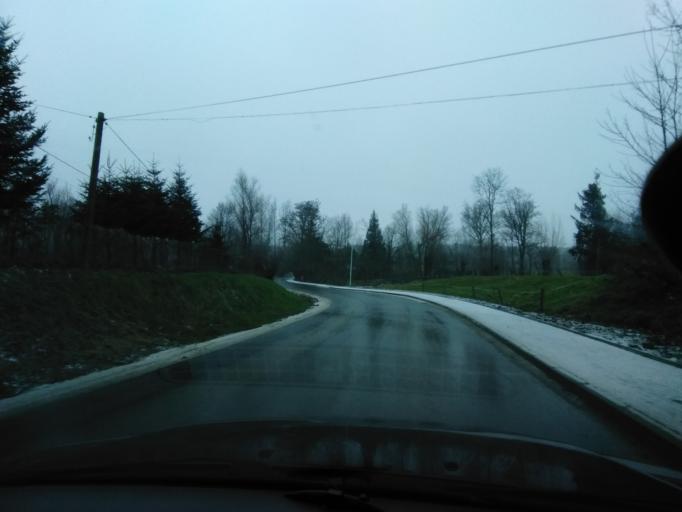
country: PL
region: Subcarpathian Voivodeship
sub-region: Powiat przeworski
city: Gac
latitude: 50.0195
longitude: 22.3932
